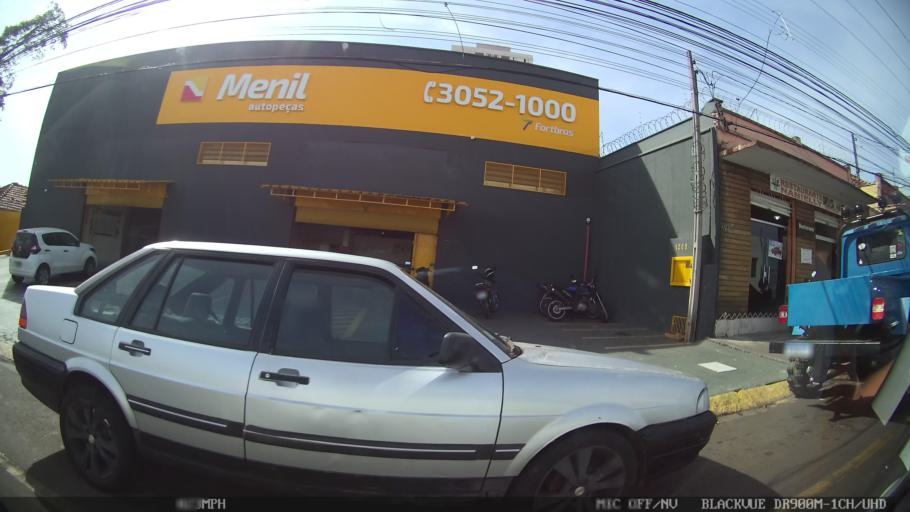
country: BR
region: Sao Paulo
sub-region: Piracicaba
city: Piracicaba
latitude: -22.7493
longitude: -47.6495
